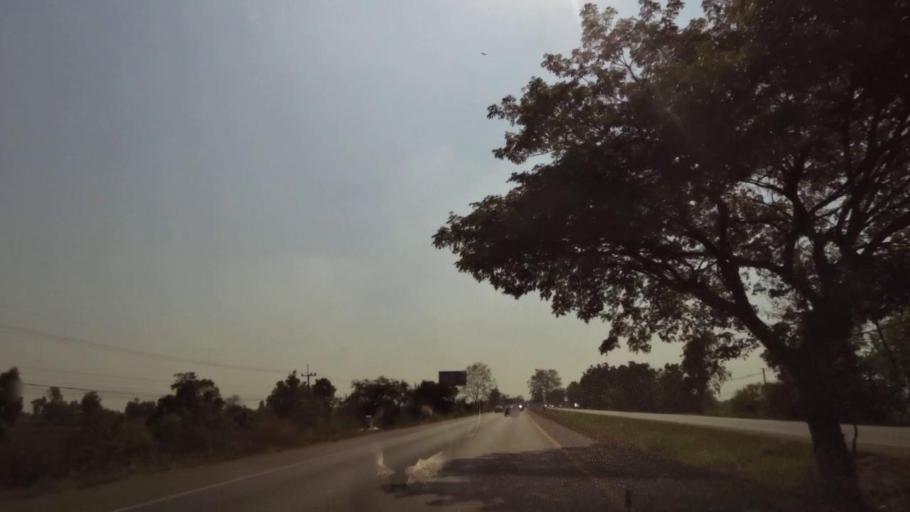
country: TH
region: Phichit
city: Wachira Barami
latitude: 16.4679
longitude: 100.1474
